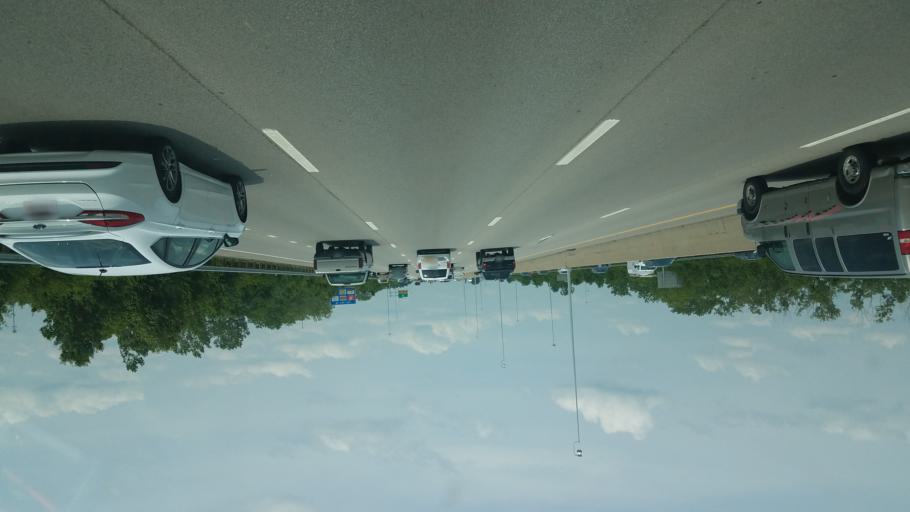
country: US
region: Ohio
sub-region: Franklin County
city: Huber Ridge
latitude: 40.1022
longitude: -82.9337
